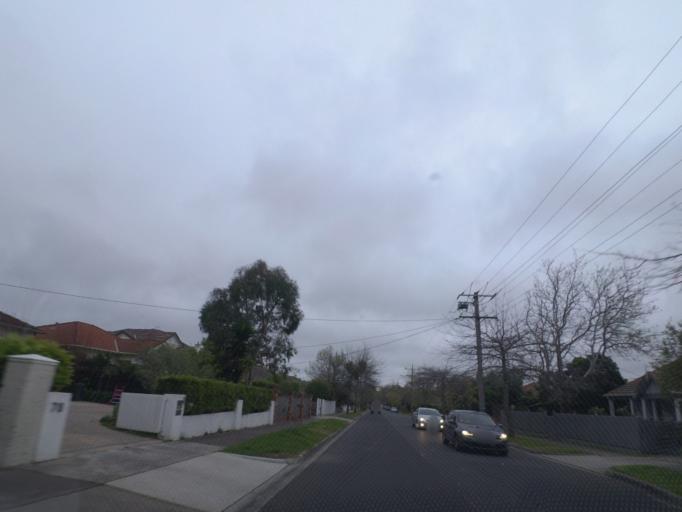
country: AU
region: Victoria
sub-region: Boroondara
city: Ashburton
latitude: -37.8681
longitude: 145.0691
